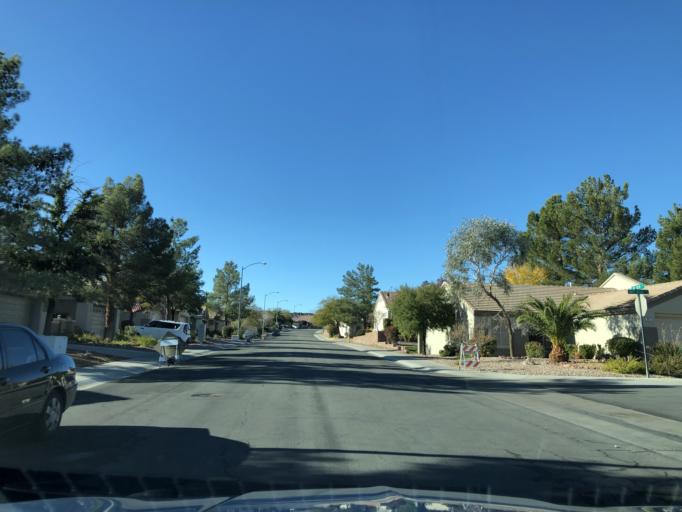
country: US
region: Nevada
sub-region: Clark County
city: Whitney
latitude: 36.0069
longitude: -115.0701
